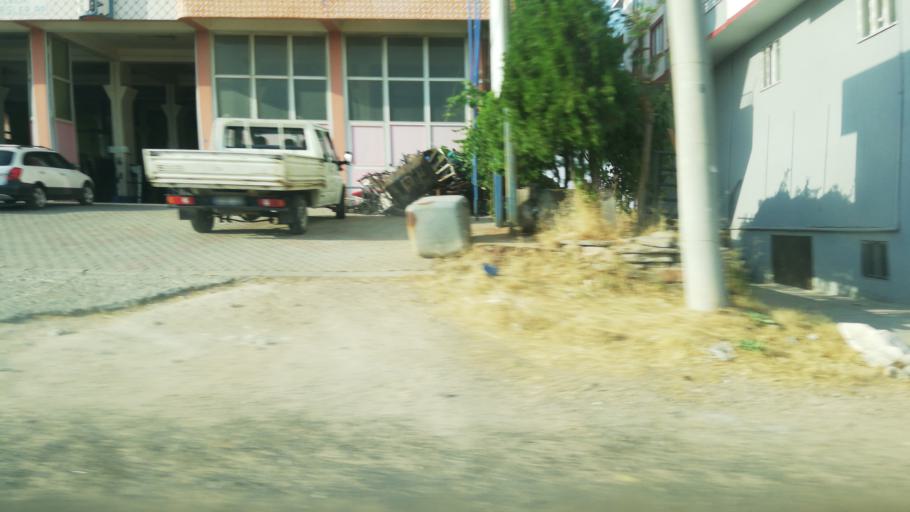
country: TR
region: Mardin
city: Midyat
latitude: 37.4364
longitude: 41.3188
